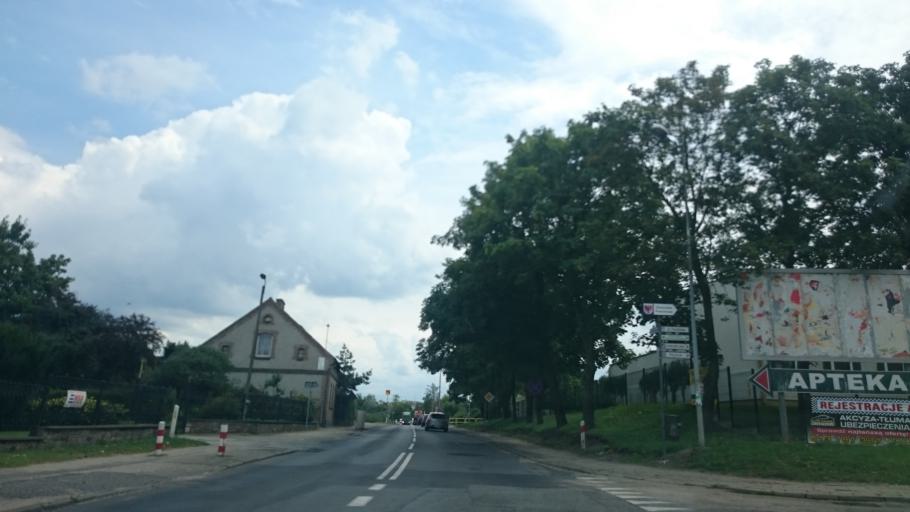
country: PL
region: Kujawsko-Pomorskie
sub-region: Powiat tucholski
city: Tuchola
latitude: 53.5894
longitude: 17.8669
